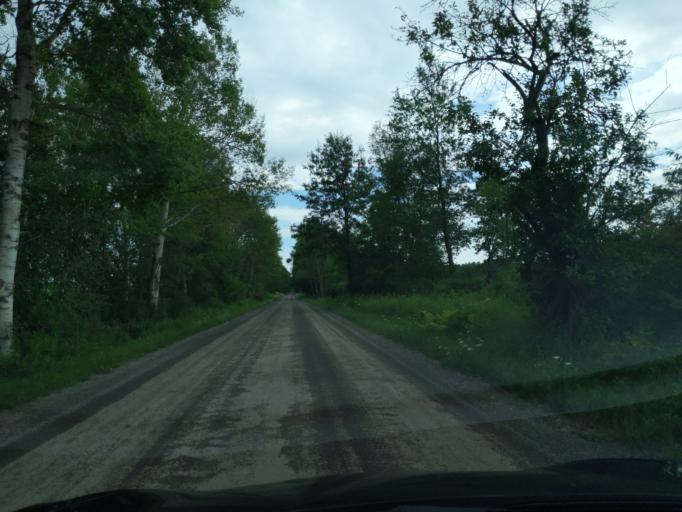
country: US
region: Michigan
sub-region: Clare County
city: Harrison
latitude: 43.9847
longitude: -84.9983
